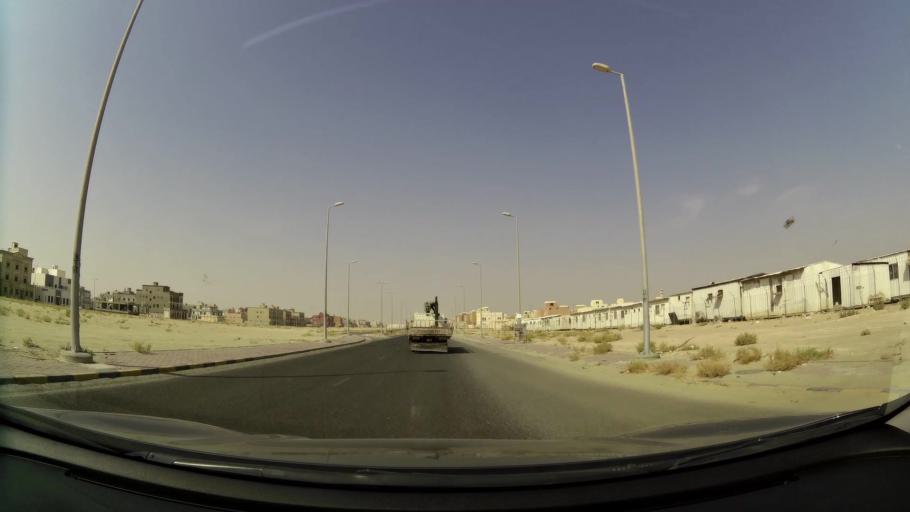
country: KW
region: Al Ahmadi
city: Al Wafrah
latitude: 28.7981
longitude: 48.0597
